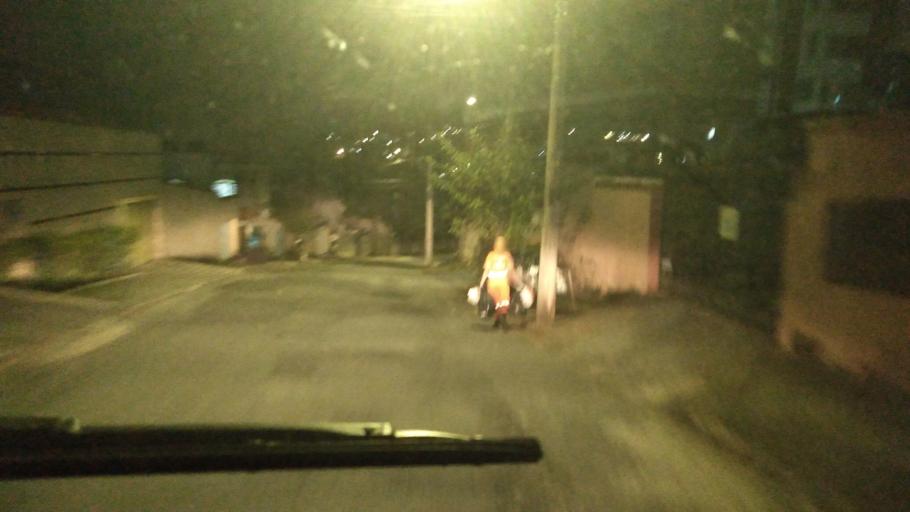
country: BR
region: Minas Gerais
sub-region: Belo Horizonte
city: Belo Horizonte
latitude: -19.8721
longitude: -43.9437
